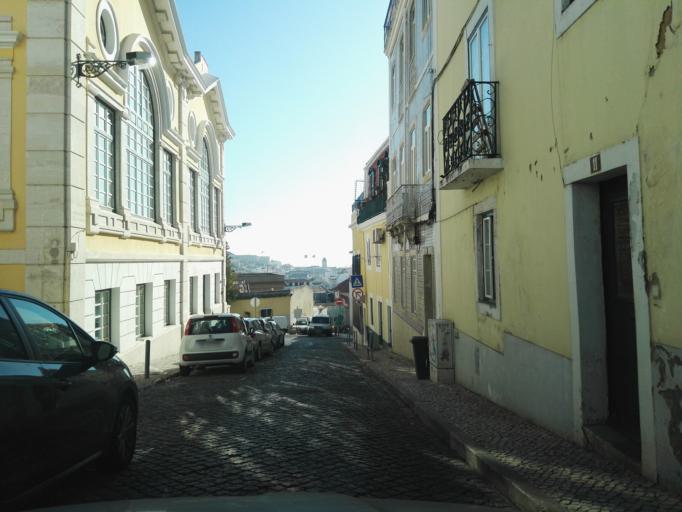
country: PT
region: Lisbon
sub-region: Lisbon
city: Lisbon
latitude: 38.7095
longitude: -9.1553
